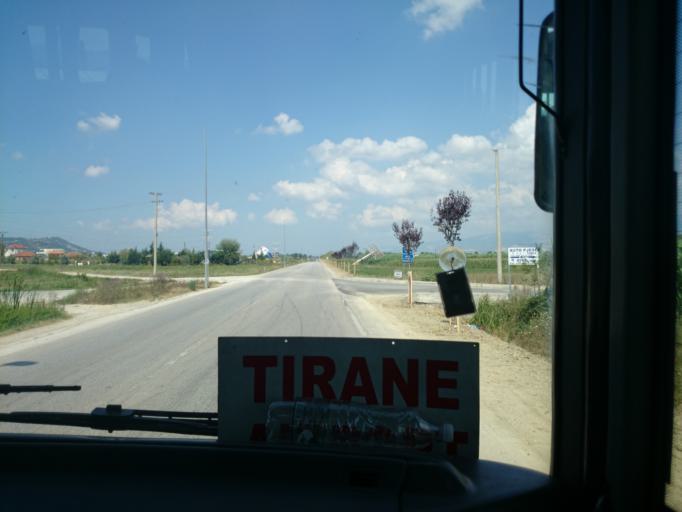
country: AL
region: Tirane
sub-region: Rrethi i Tiranes
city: Berxull
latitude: 41.3787
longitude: 19.7037
